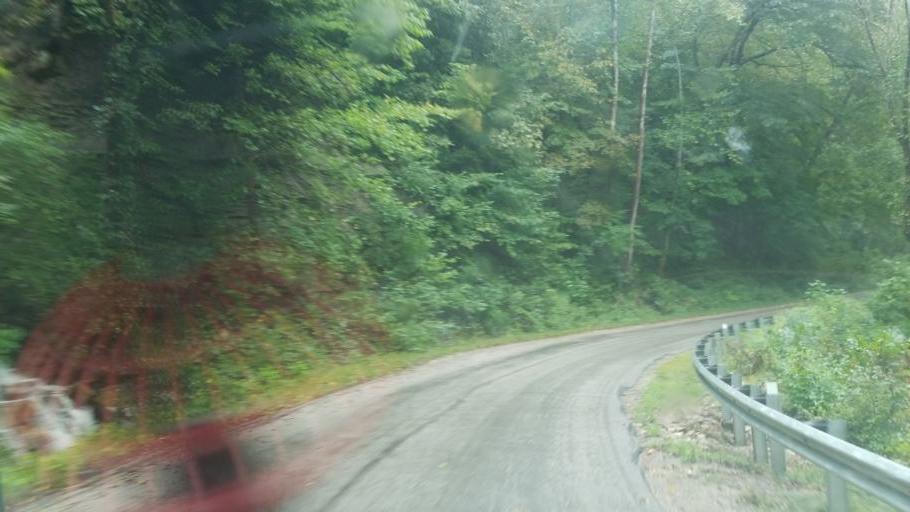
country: US
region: Kentucky
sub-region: Lewis County
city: Vanceburg
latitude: 38.7802
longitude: -83.2566
